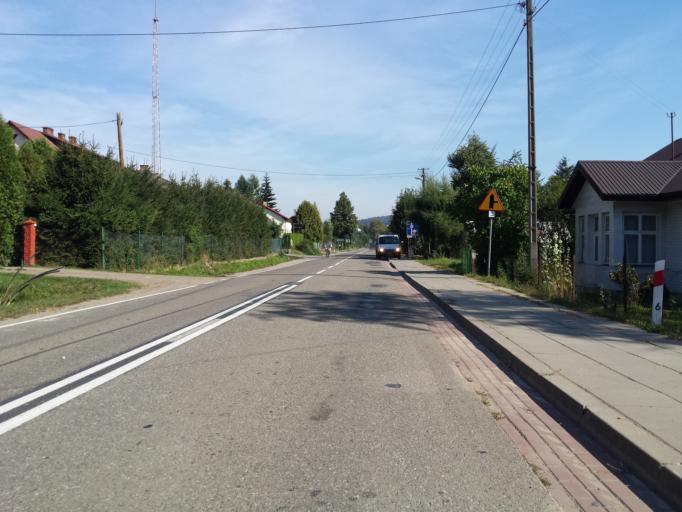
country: PL
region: Subcarpathian Voivodeship
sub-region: Powiat leski
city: Baligrod
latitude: 49.3297
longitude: 22.2852
